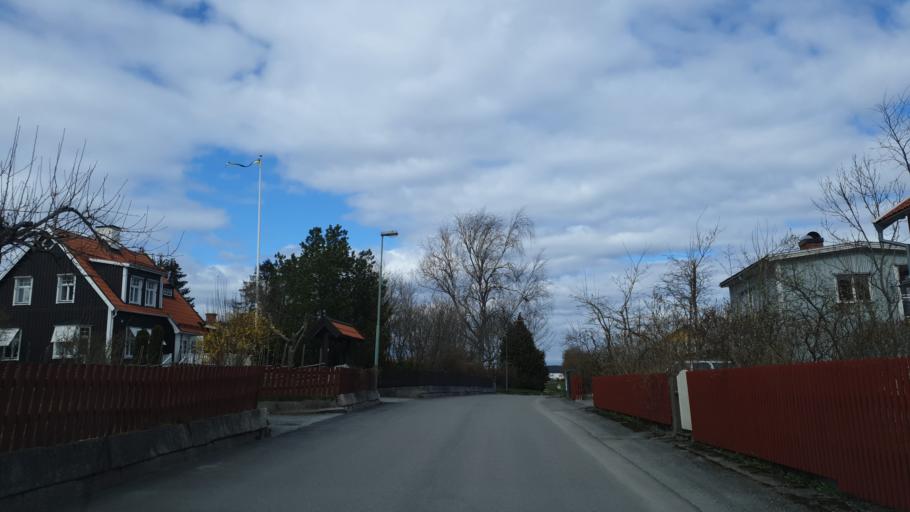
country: SE
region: OErebro
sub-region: Nora Kommun
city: Nora
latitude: 59.5246
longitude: 15.0428
